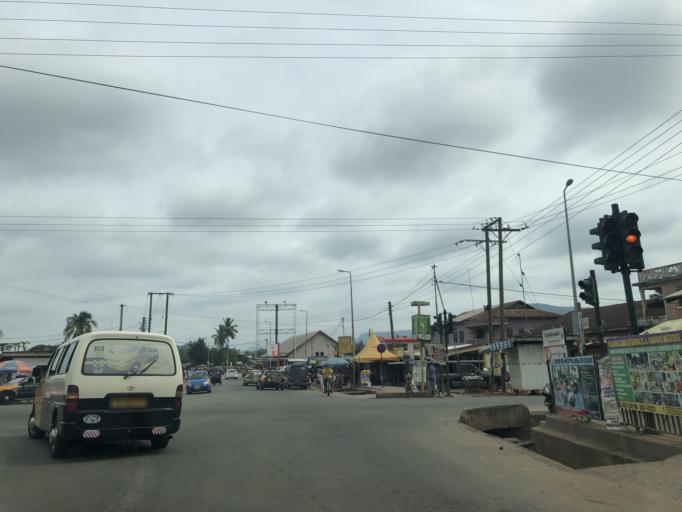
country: GH
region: Eastern
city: Koforidua
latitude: 6.1117
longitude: -0.2690
